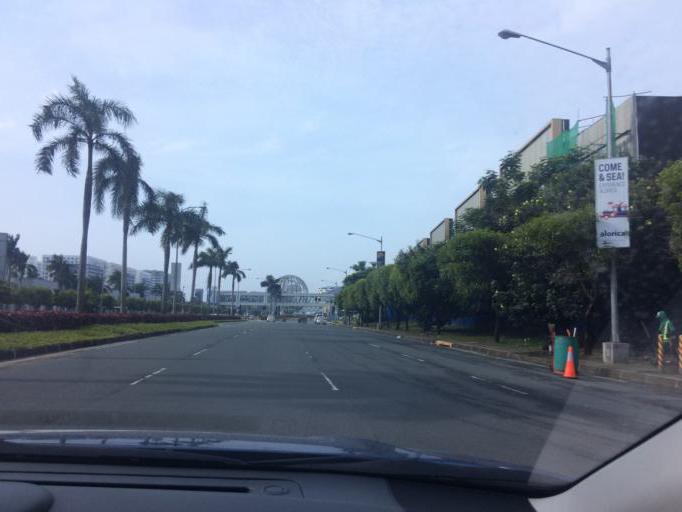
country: PH
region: Metro Manila
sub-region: City of Manila
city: Port Area
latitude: 14.5389
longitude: 120.9838
